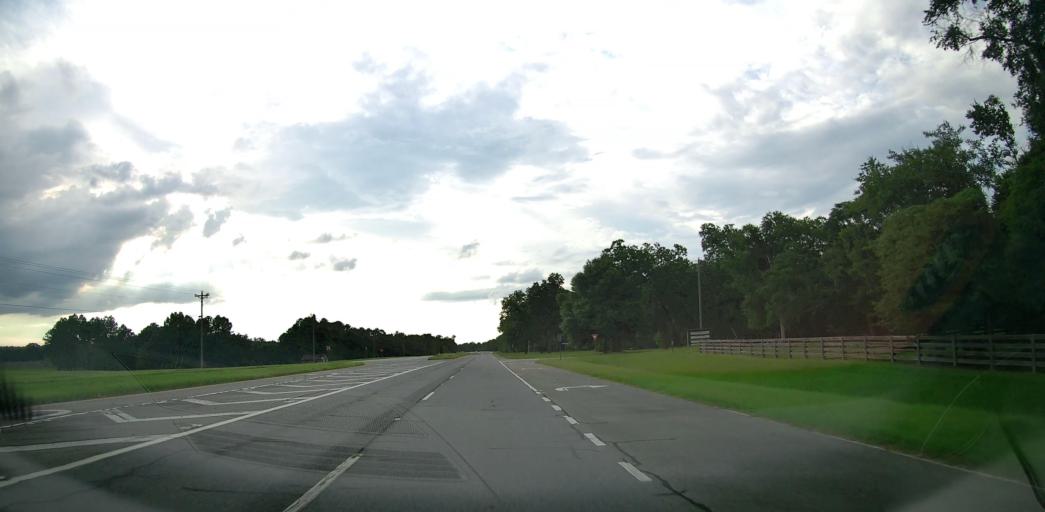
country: US
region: Georgia
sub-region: Pulaski County
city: Hawkinsville
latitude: 32.2734
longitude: -83.4203
